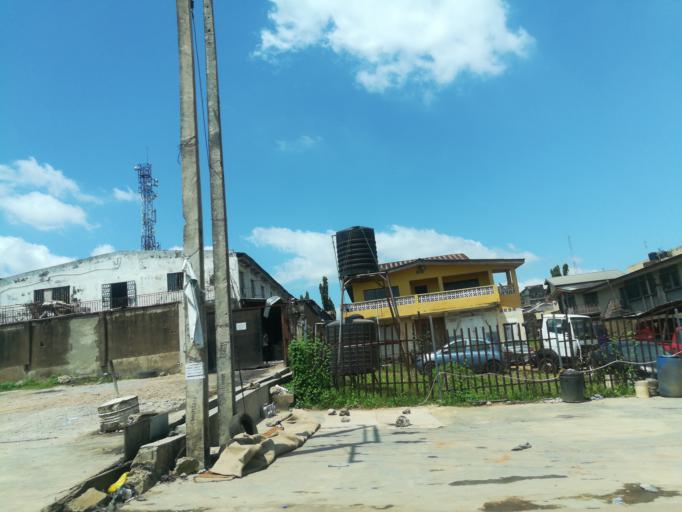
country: NG
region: Oyo
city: Ibadan
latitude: 7.3583
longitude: 3.8688
